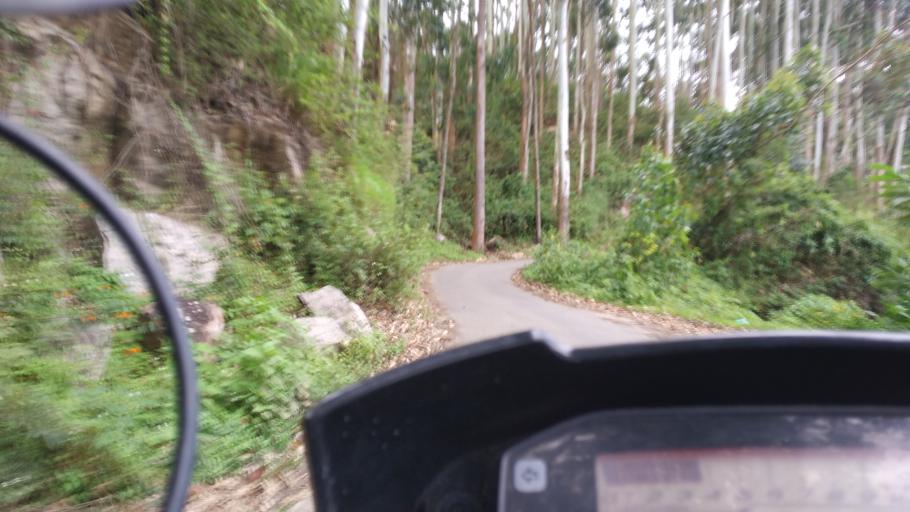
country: IN
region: Kerala
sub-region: Idukki
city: Munnar
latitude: 10.0359
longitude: 77.1706
